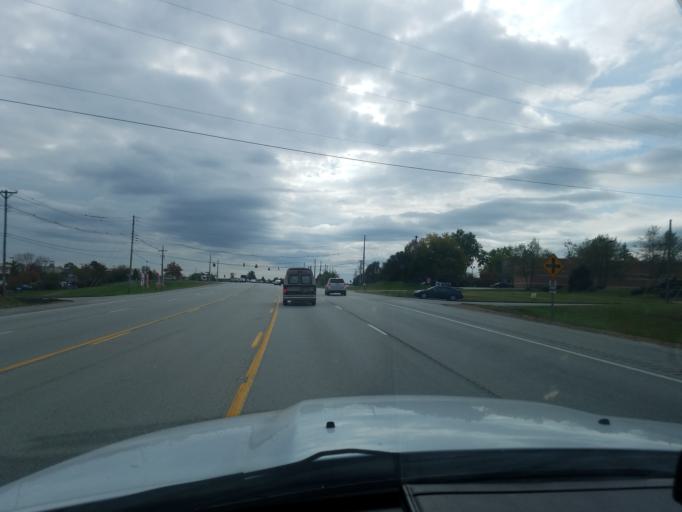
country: US
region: Kentucky
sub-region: Jefferson County
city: Fern Creek
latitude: 38.1321
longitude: -85.5788
